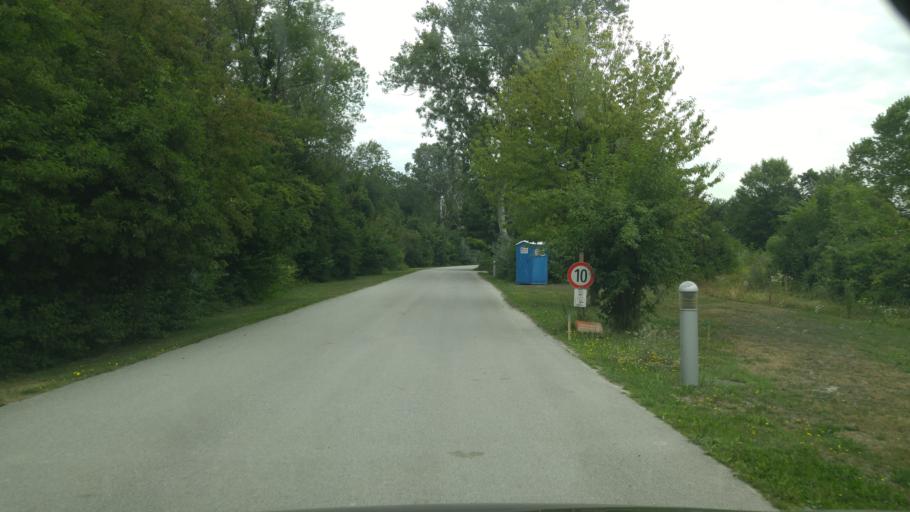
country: AT
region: Lower Austria
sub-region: Politischer Bezirk Wien-Umgebung
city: Moosbrunn
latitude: 48.0392
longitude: 16.4355
